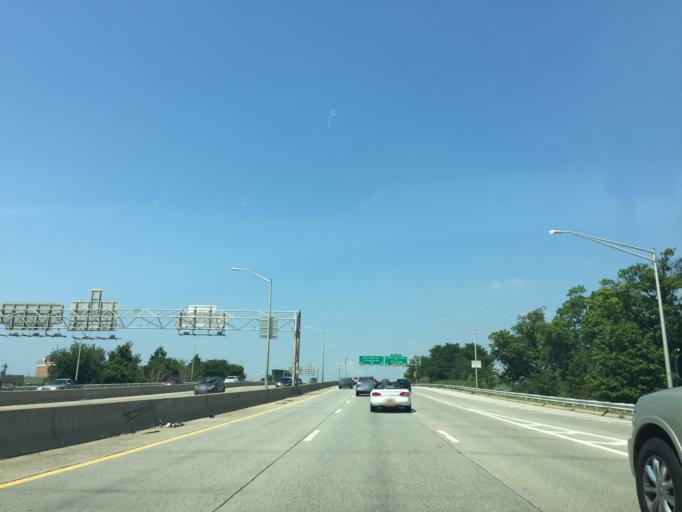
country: US
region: New York
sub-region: Queens County
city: Jamaica
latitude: 40.6675
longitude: -73.7775
